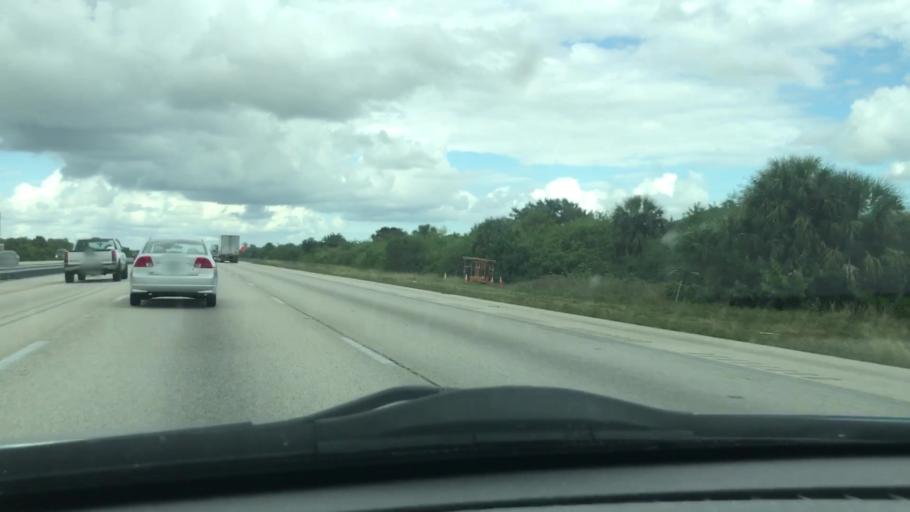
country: US
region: Florida
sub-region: Brevard County
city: Rockledge
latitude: 28.2510
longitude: -80.7242
